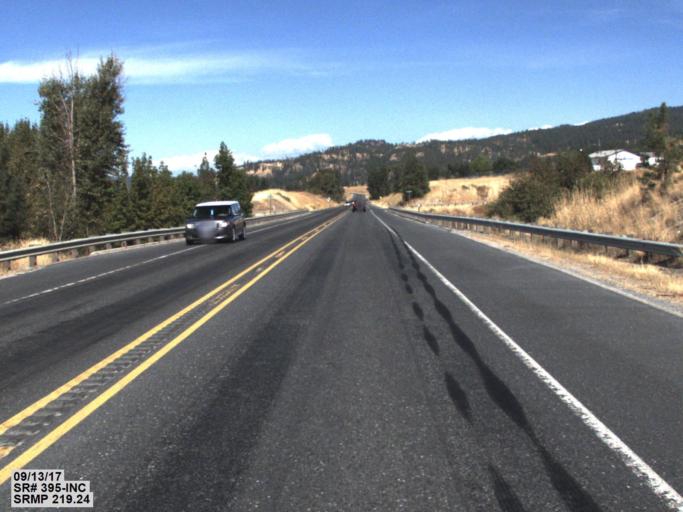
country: US
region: Washington
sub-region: Stevens County
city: Colville
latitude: 48.4052
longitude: -117.8505
